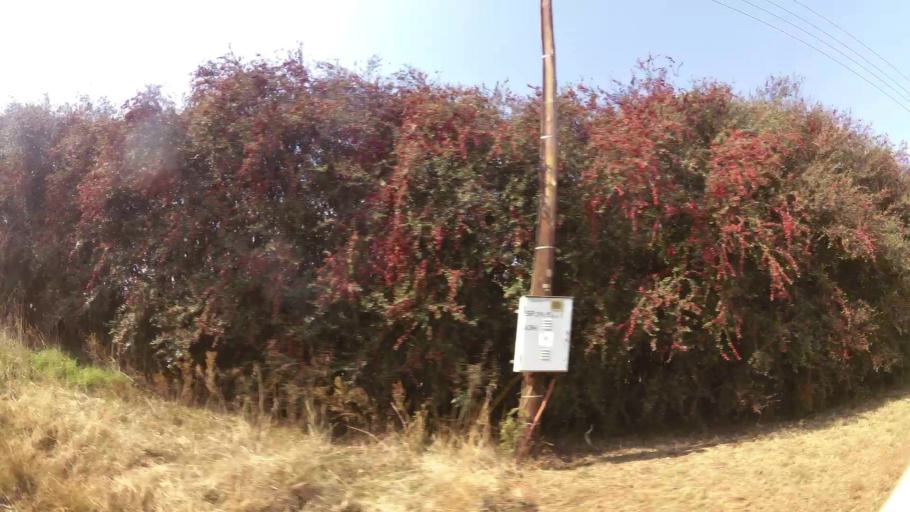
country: ZA
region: Gauteng
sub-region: Ekurhuleni Metropolitan Municipality
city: Springs
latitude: -26.2036
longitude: 28.5389
